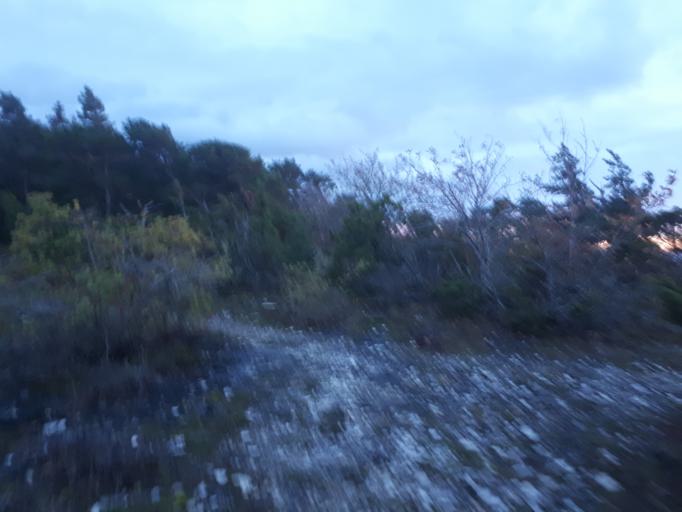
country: SE
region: Gotland
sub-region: Gotland
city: Visby
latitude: 57.6834
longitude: 18.3466
